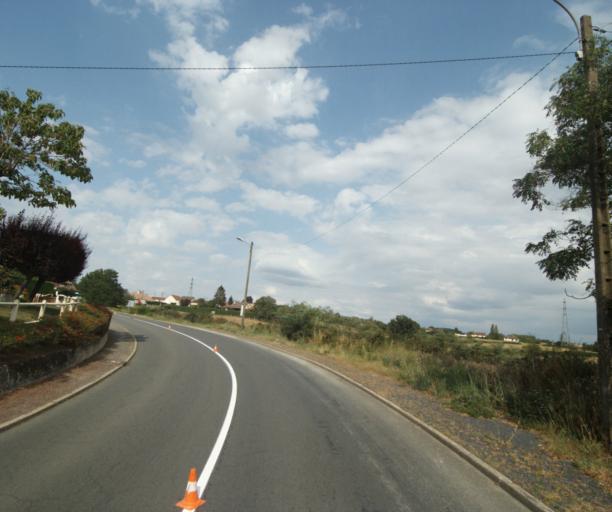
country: FR
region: Bourgogne
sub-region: Departement de Saone-et-Loire
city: Gueugnon
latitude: 46.6017
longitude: 4.0809
